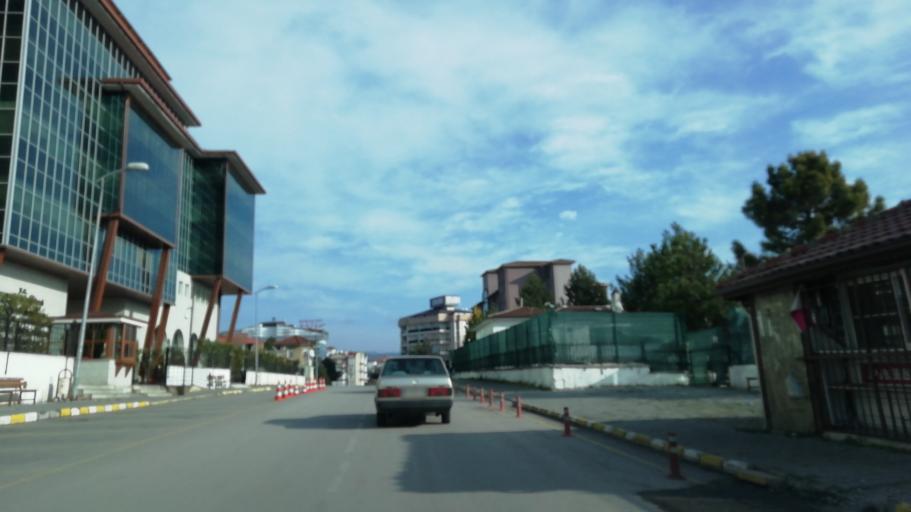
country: TR
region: Karabuk
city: Safranbolu
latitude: 41.2537
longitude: 32.6754
